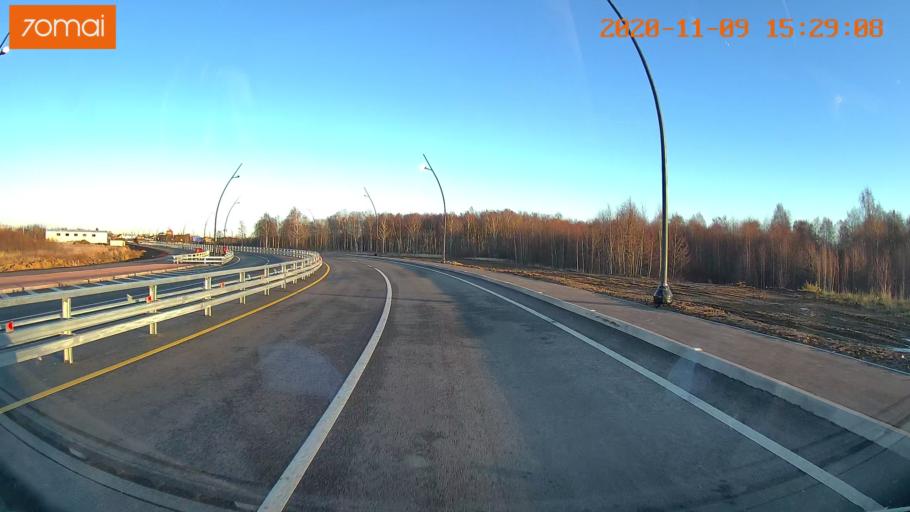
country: RU
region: Ivanovo
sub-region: Gorod Ivanovo
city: Ivanovo
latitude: 56.9509
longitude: 40.9396
